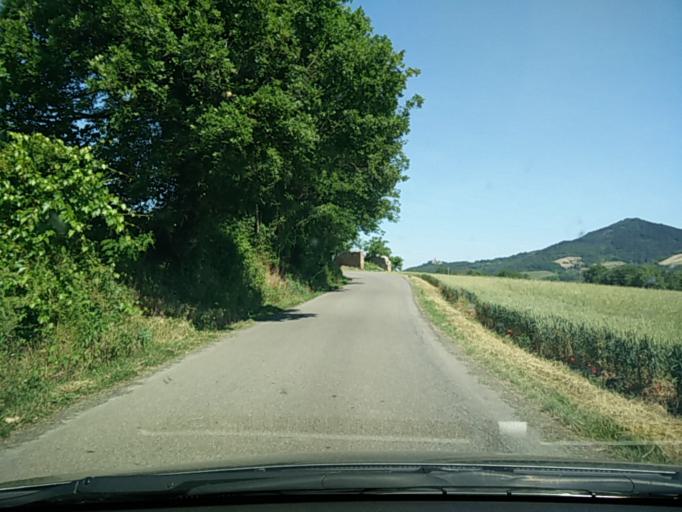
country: IT
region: Lombardy
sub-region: Provincia di Pavia
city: Godiasco
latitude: 44.8957
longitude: 9.0494
